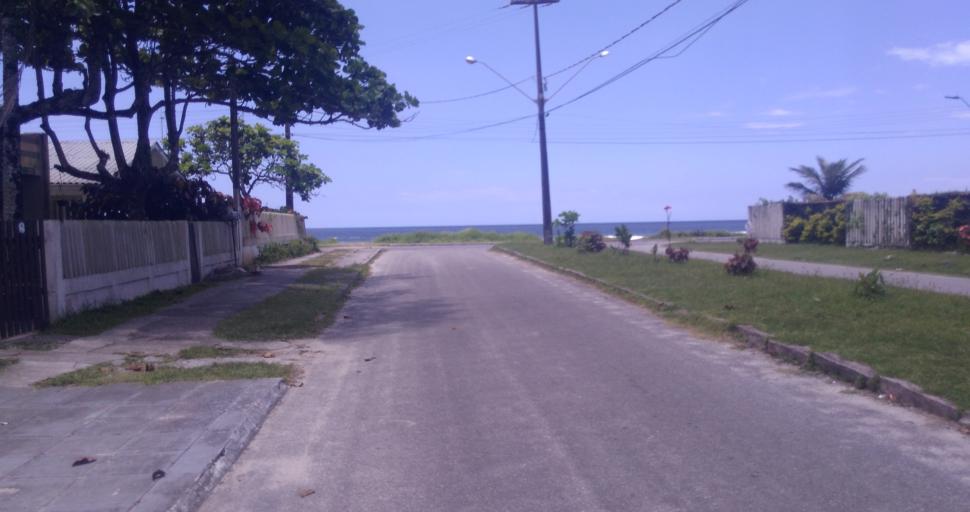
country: BR
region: Parana
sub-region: Pontal Do Parana
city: Pontal do Parana
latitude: -25.7648
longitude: -48.5090
